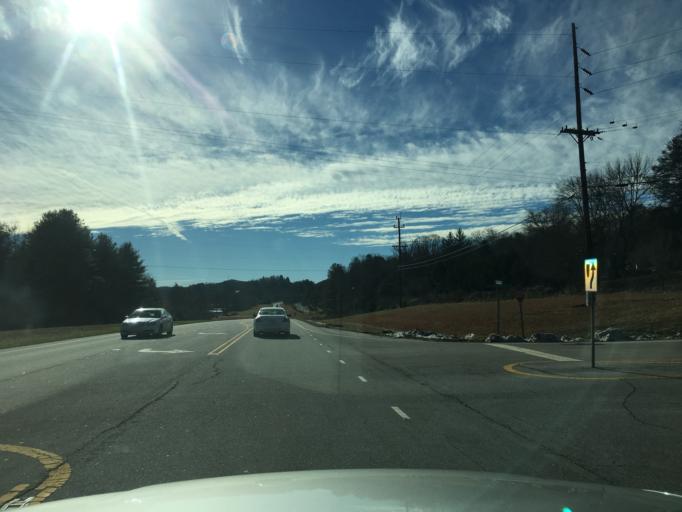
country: US
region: North Carolina
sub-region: Transylvania County
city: Brevard
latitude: 35.1742
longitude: -82.8038
